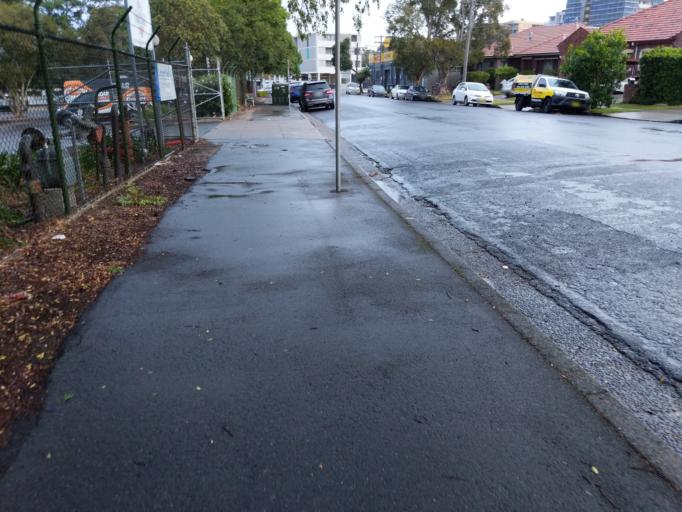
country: AU
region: New South Wales
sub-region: Ashfield
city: Croydon
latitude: -33.8683
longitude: 151.1083
